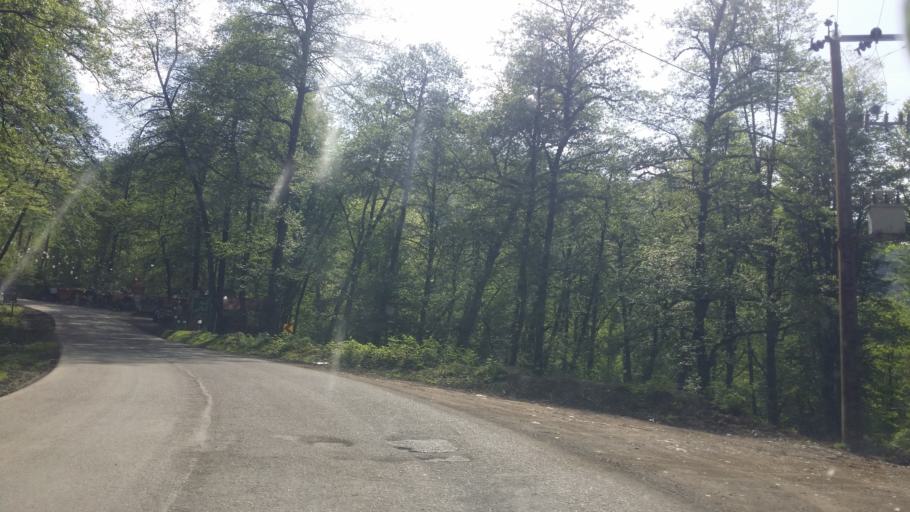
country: IR
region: Mazandaran
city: `Abbasabad
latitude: 36.6294
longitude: 51.1076
